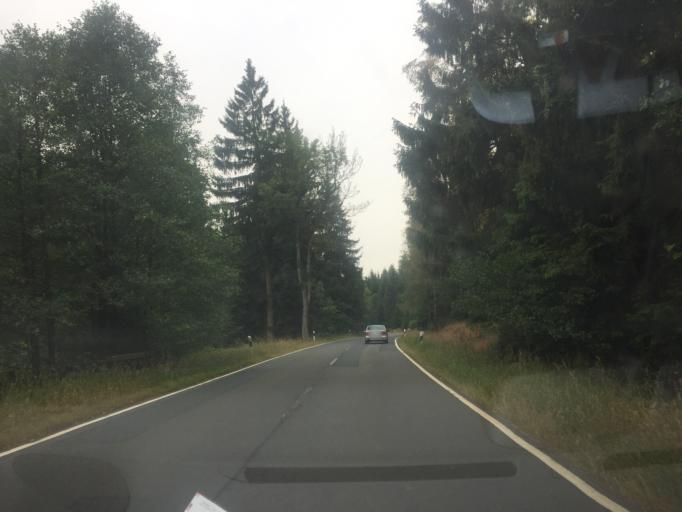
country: DE
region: Lower Saxony
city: Wieda
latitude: 51.6769
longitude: 10.5982
